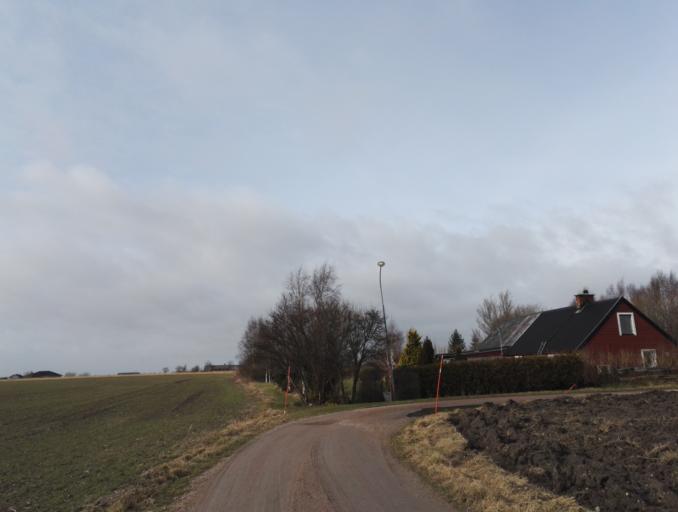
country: SE
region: Skane
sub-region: Landskrona
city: Asmundtorp
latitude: 55.8933
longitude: 13.0020
